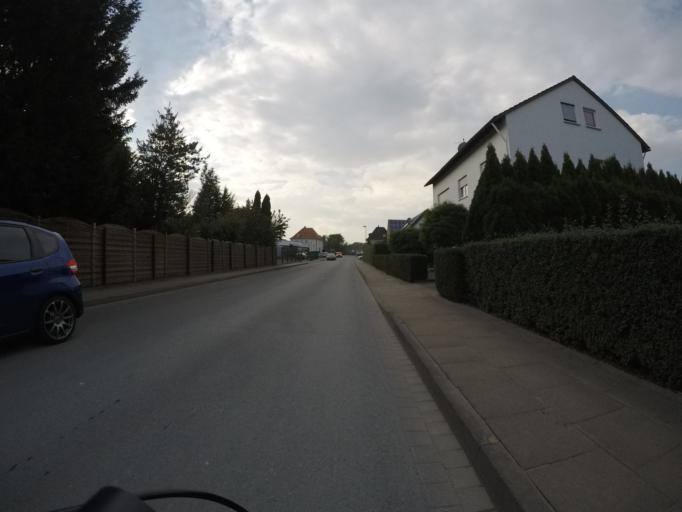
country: DE
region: North Rhine-Westphalia
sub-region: Regierungsbezirk Detmold
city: Bielefeld
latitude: 52.0624
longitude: 8.6089
